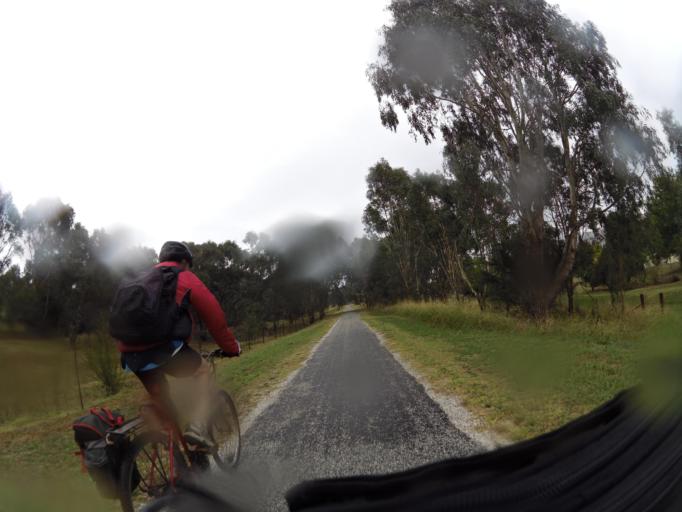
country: AU
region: New South Wales
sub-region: Albury Municipality
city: East Albury
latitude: -36.2174
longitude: 147.1876
